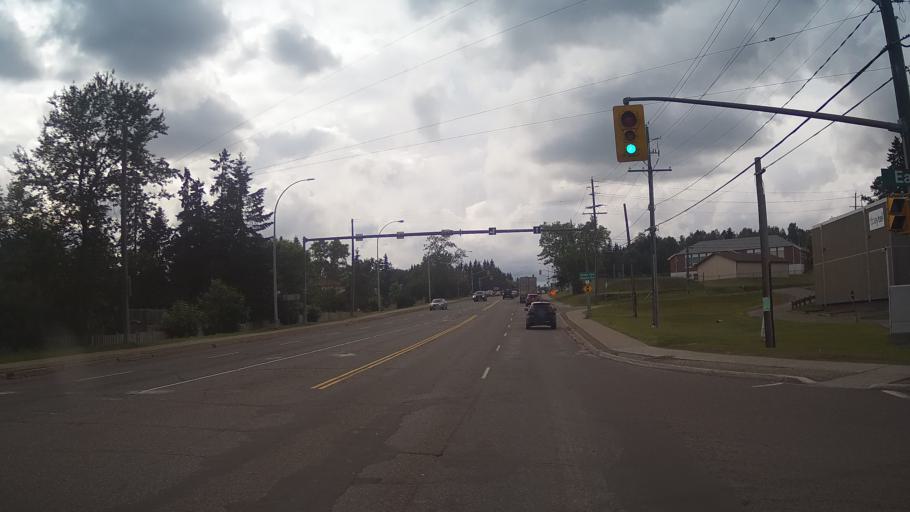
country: CA
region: Ontario
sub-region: Thunder Bay District
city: Thunder Bay
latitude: 48.4527
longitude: -89.2568
